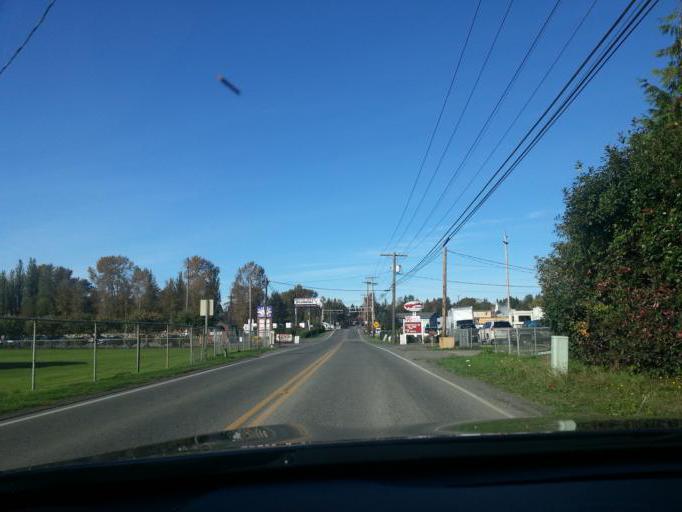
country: US
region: Washington
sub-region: Snohomish County
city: Snohomish
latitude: 47.9062
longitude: -122.0986
